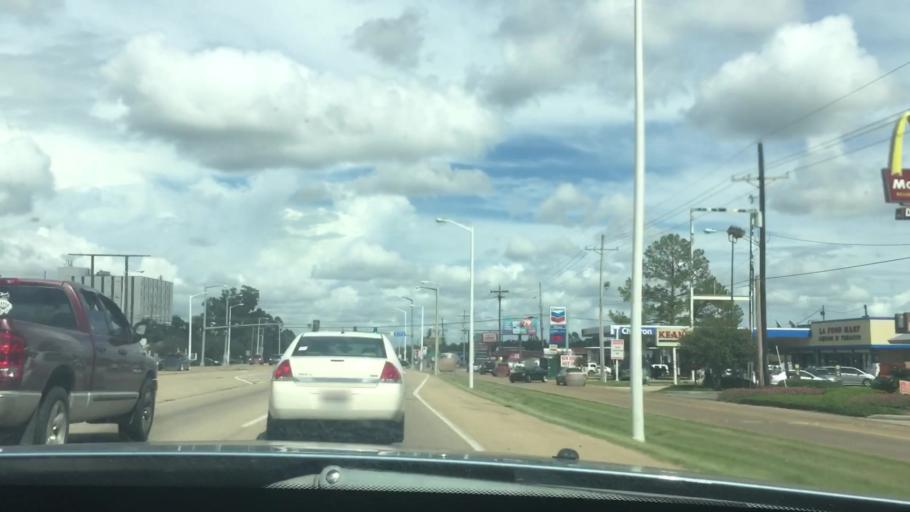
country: US
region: Louisiana
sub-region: East Baton Rouge Parish
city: Monticello
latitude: 30.4562
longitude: -91.0751
